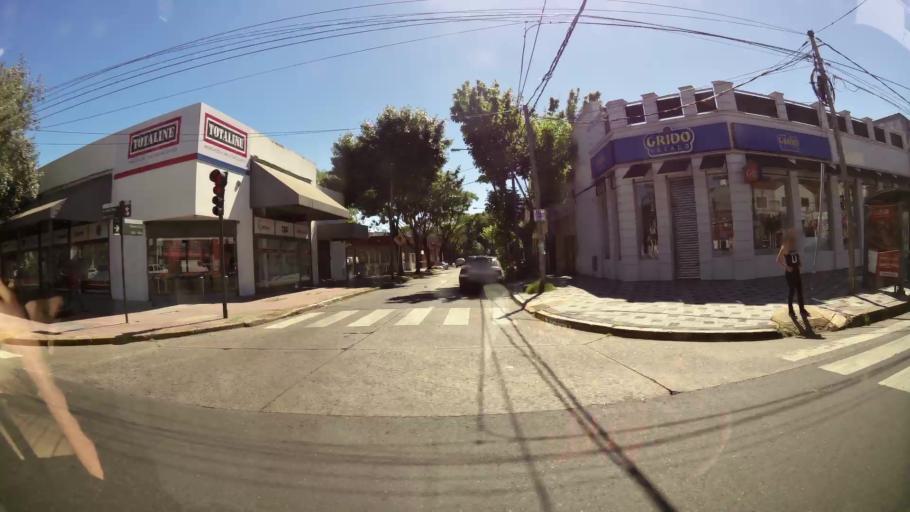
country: AR
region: Buenos Aires
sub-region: Partido de Vicente Lopez
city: Olivos
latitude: -34.5258
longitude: -58.5192
